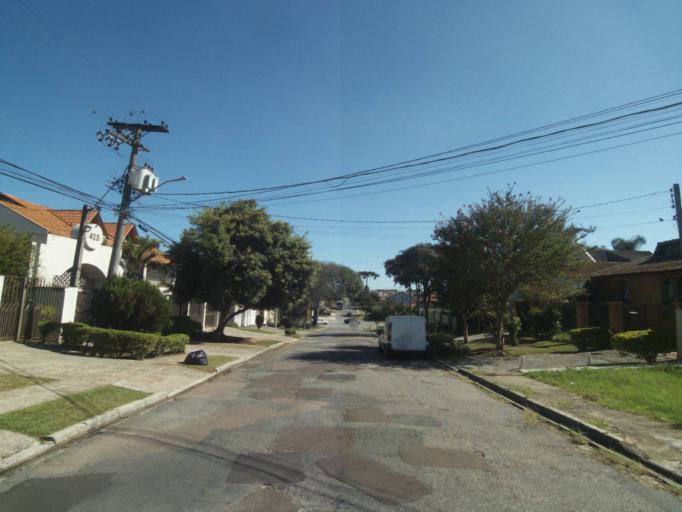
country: BR
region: Parana
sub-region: Pinhais
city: Pinhais
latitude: -25.4378
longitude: -49.2302
